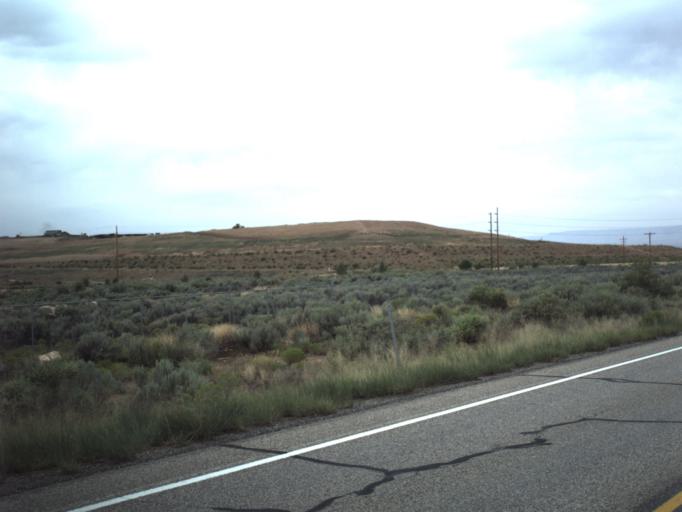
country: US
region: Utah
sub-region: Carbon County
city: East Carbon City
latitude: 39.5356
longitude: -110.4736
